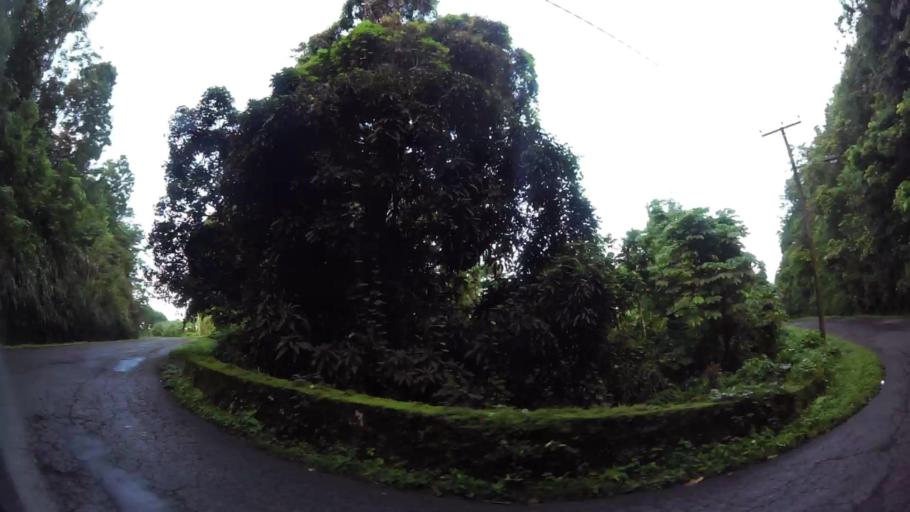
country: LC
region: Anse-la-Raye
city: Canaries
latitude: 13.9168
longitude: -61.0425
